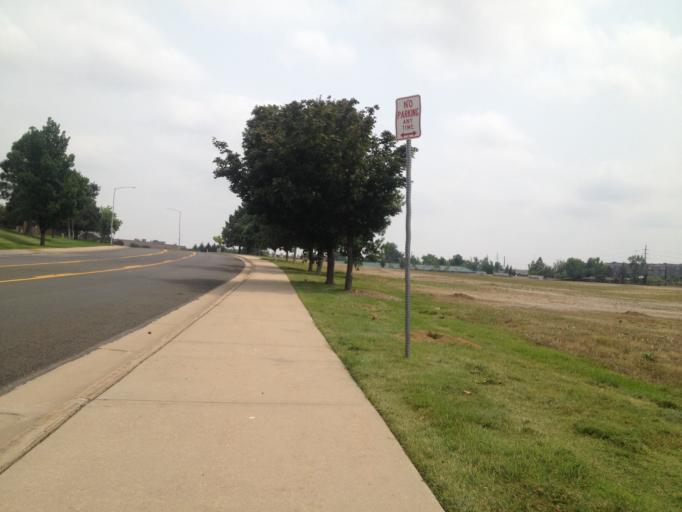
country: US
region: Colorado
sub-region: Broomfield County
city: Broomfield
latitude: 39.9251
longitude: -105.1057
